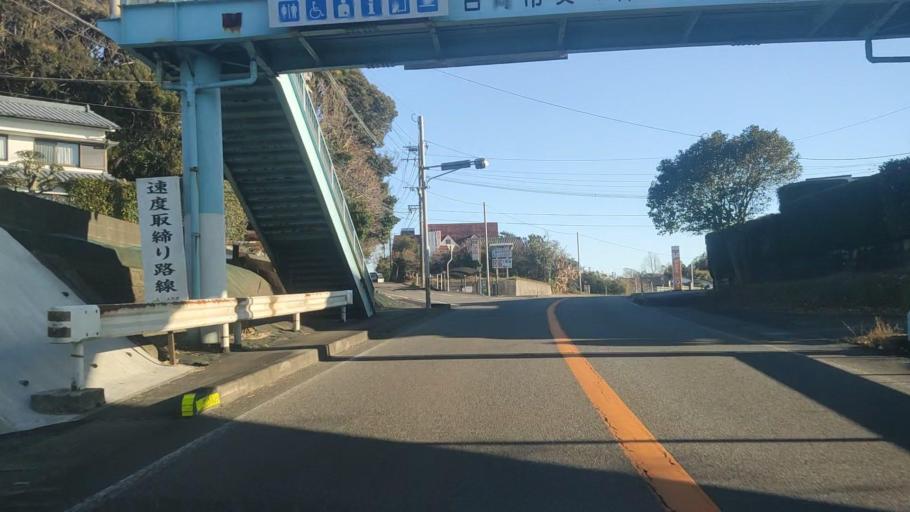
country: JP
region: Miyazaki
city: Takanabe
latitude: 32.3317
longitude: 131.6046
